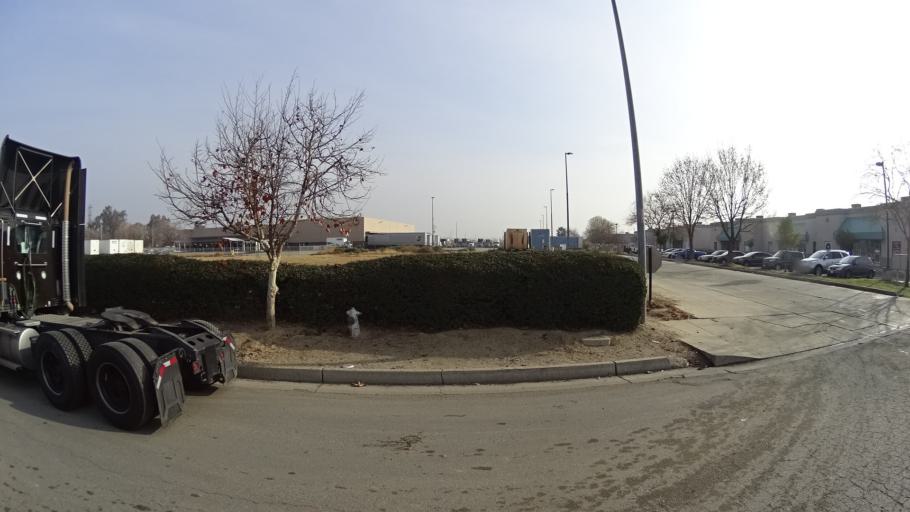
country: US
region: California
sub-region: Kern County
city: Bakersfield
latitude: 35.3943
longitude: -119.0362
